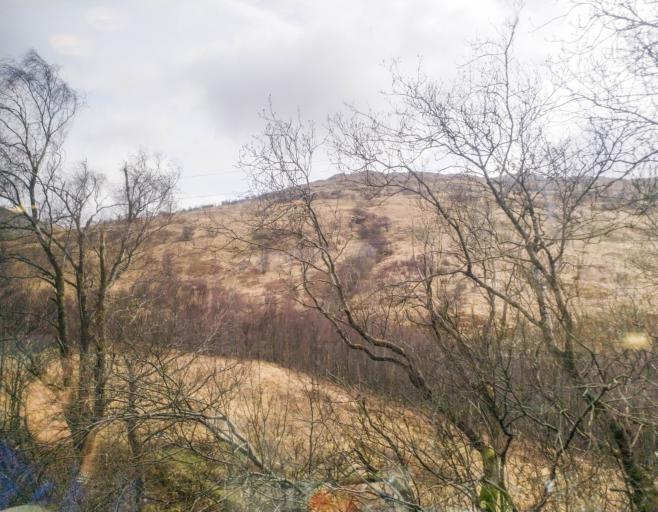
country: GB
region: Scotland
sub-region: Argyll and Bute
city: Garelochhead
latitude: 56.3515
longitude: -4.6922
